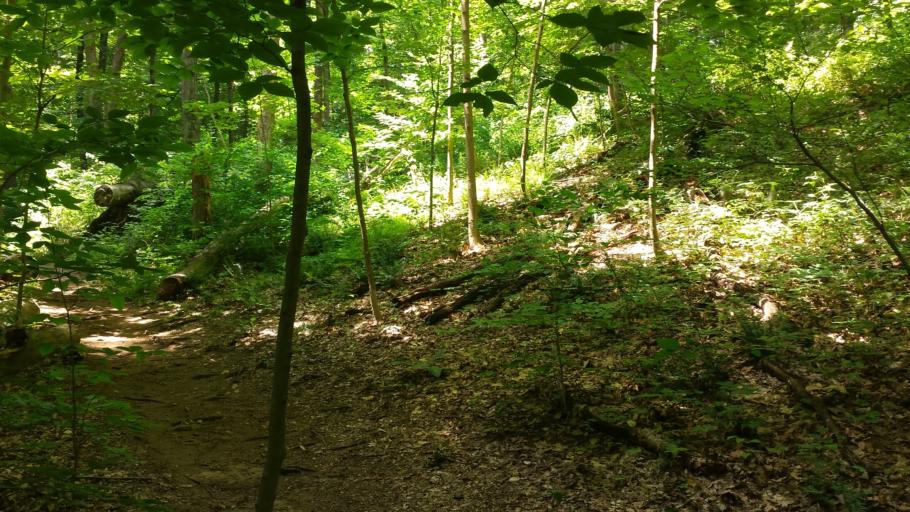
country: US
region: New York
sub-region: Westchester County
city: Yorktown Heights
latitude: 41.2235
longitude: -73.7856
